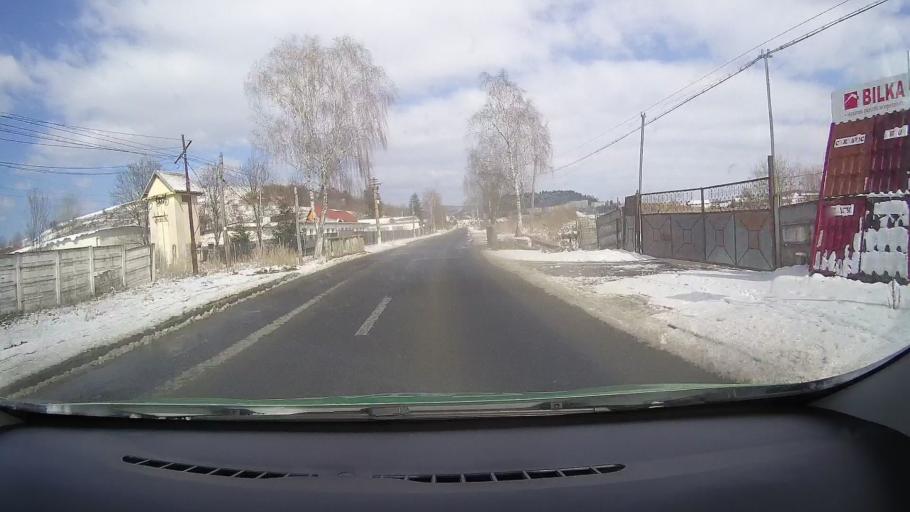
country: RO
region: Sibiu
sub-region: Oras Agnita
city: Agnita
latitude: 45.9709
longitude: 24.6062
